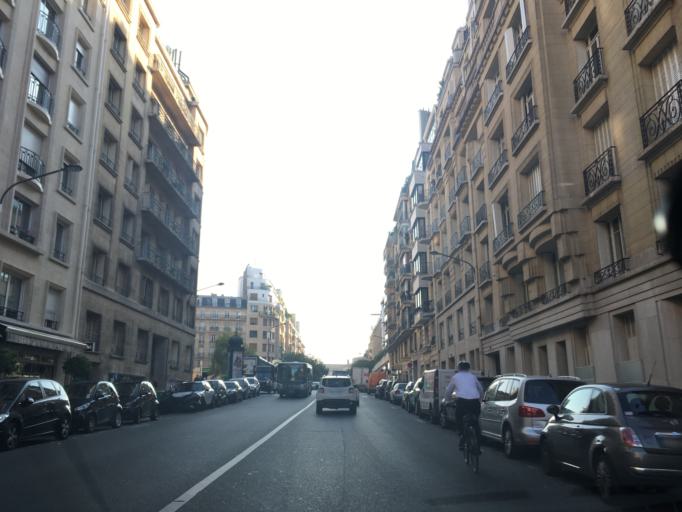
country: FR
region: Ile-de-France
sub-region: Departement des Hauts-de-Seine
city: Neuilly-sur-Seine
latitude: 48.8604
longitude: 2.2816
